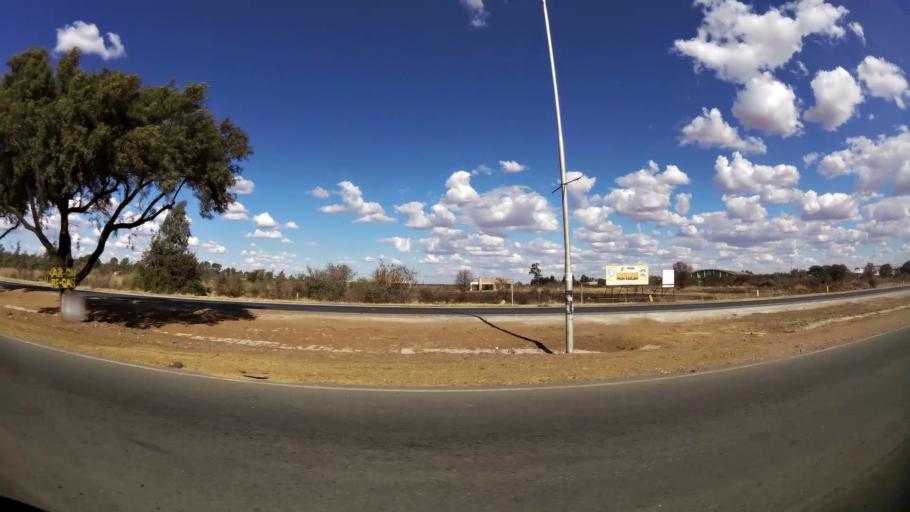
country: ZA
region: North-West
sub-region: Dr Kenneth Kaunda District Municipality
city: Klerksdorp
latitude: -26.8677
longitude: 26.6301
